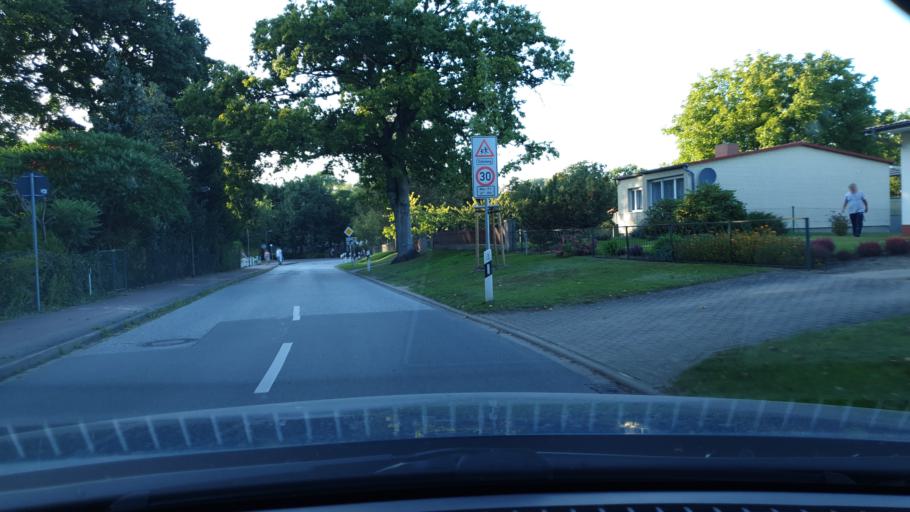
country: DE
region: Mecklenburg-Vorpommern
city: Wittenburg
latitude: 53.4996
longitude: 11.0023
